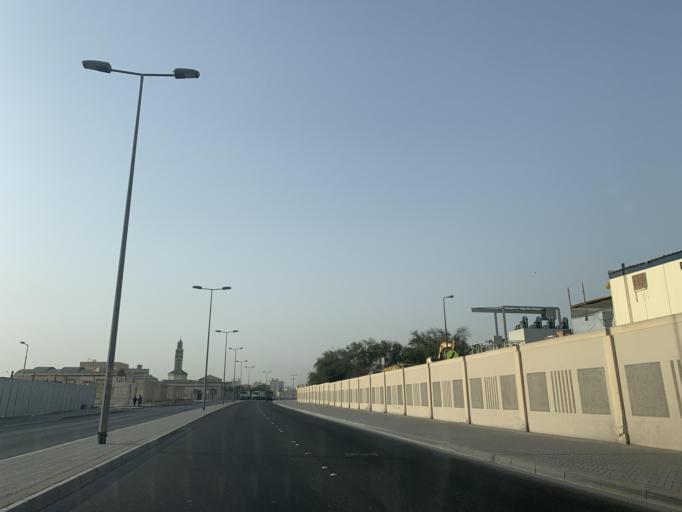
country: BH
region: Northern
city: Madinat `Isa
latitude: 26.1956
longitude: 50.5562
